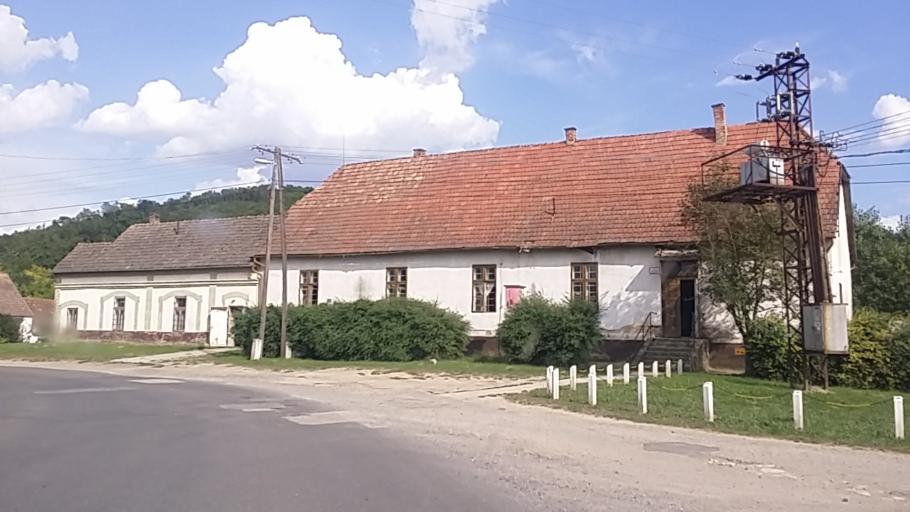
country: HU
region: Tolna
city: Zomba
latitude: 46.5002
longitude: 18.5660
